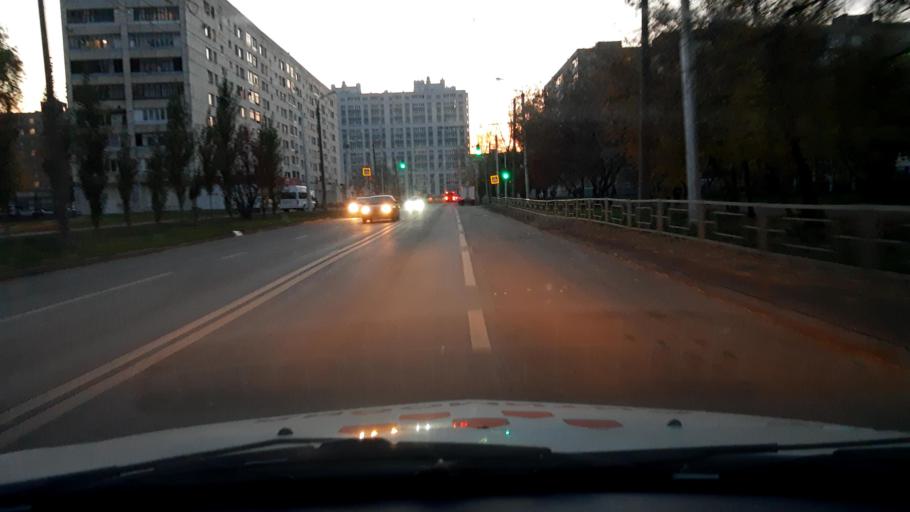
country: RU
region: Bashkortostan
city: Ufa
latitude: 54.7764
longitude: 56.1285
